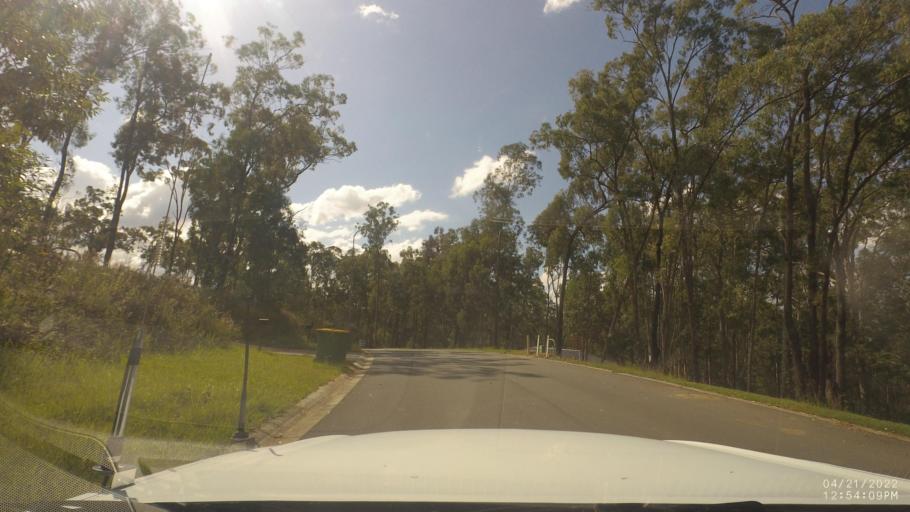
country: AU
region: Queensland
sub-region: Logan
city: Cedar Vale
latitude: -27.8364
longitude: 153.1008
